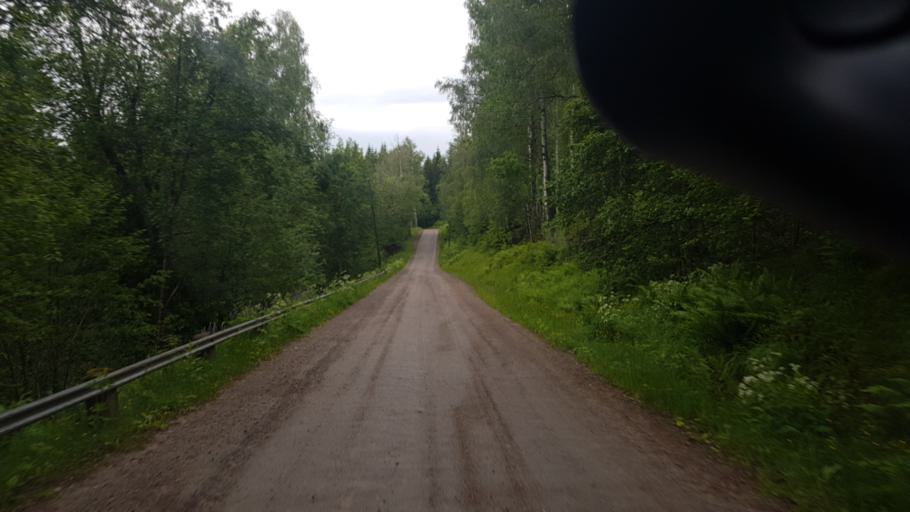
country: NO
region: Hedmark
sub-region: Eidskog
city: Skotterud
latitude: 59.7423
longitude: 12.0736
